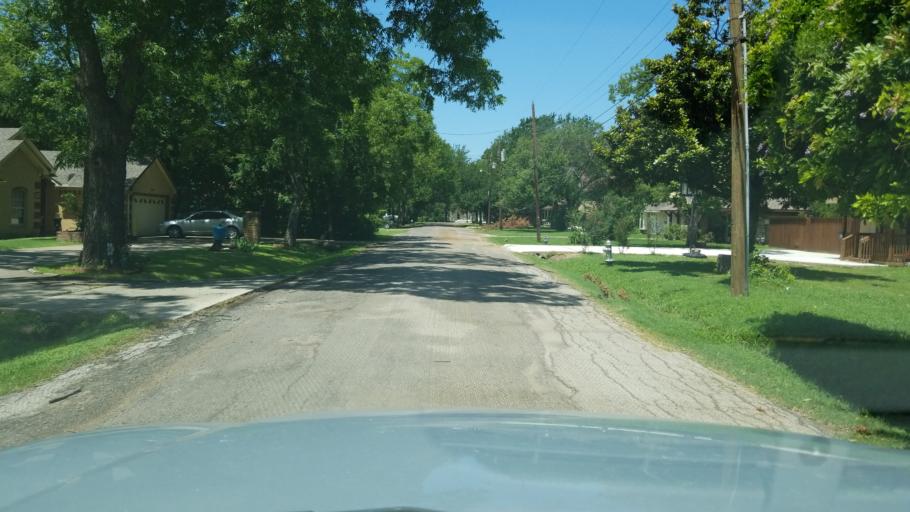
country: US
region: Texas
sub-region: Dallas County
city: Irving
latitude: 32.8023
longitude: -96.9278
